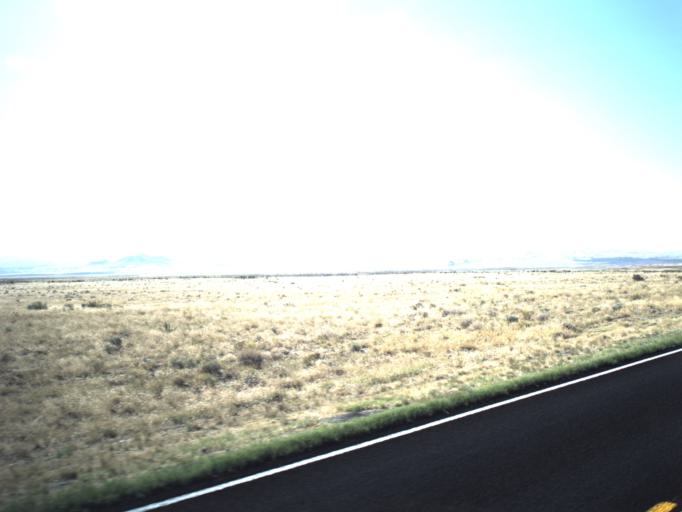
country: US
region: Utah
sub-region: Millard County
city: Fillmore
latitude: 38.9096
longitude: -112.8173
